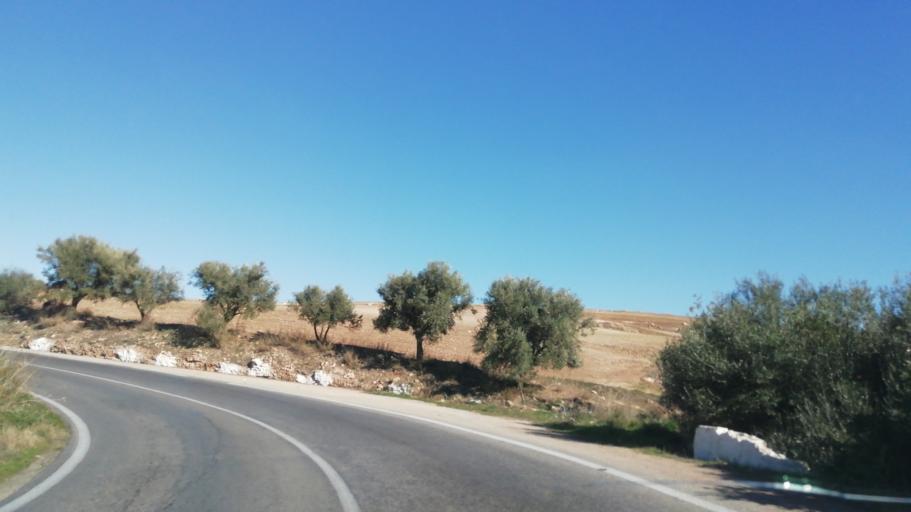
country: DZ
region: Tlemcen
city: Beni Mester
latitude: 34.8253
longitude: -1.5849
